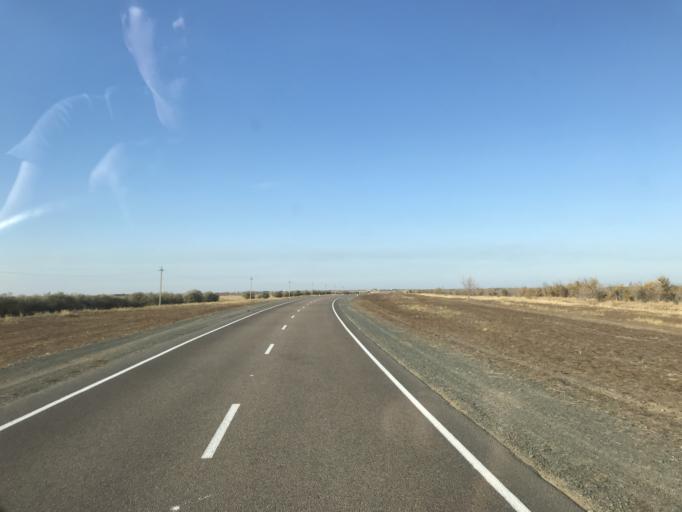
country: KZ
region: Pavlodar
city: Koktobe
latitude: 51.6129
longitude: 77.6007
